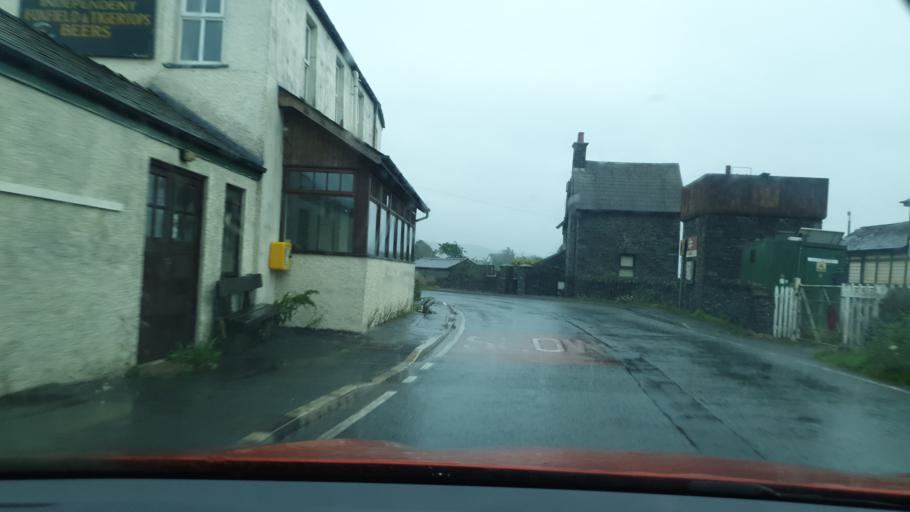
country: GB
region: England
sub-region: Cumbria
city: Millom
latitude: 54.2591
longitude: -3.2161
